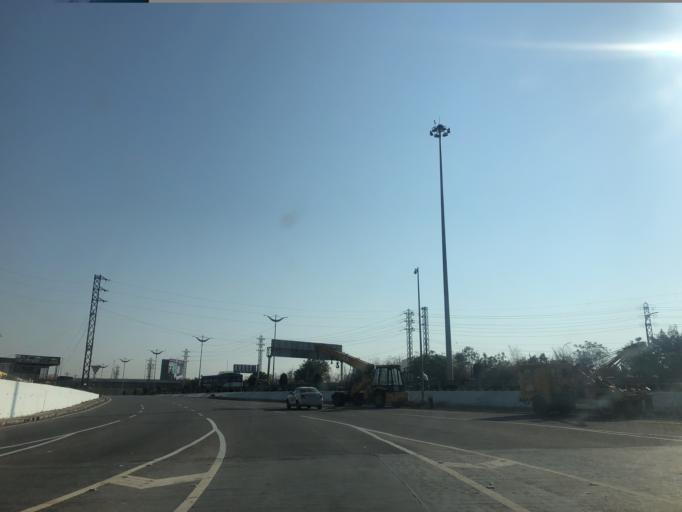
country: IN
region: Telangana
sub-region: Rangareddi
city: Sriramnagar
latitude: 17.2538
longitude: 78.3796
